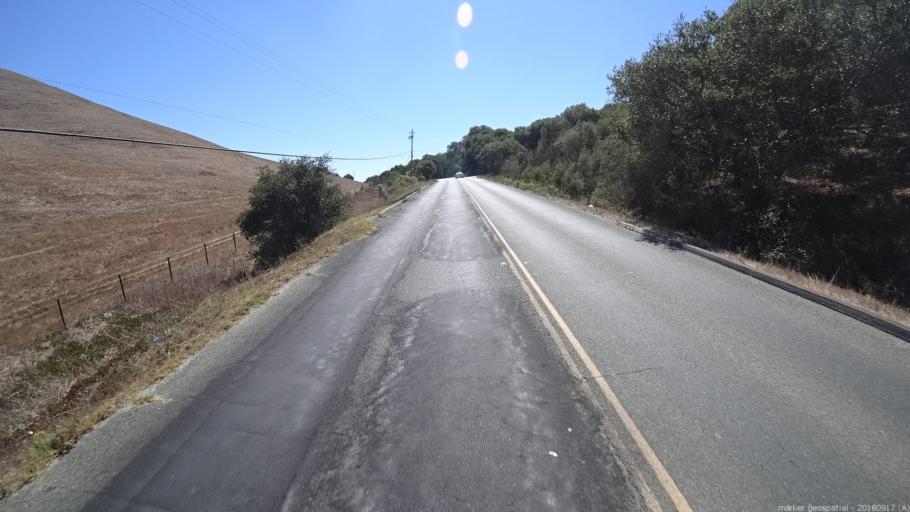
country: US
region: California
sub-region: Monterey County
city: Prunedale
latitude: 36.8116
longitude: -121.6246
